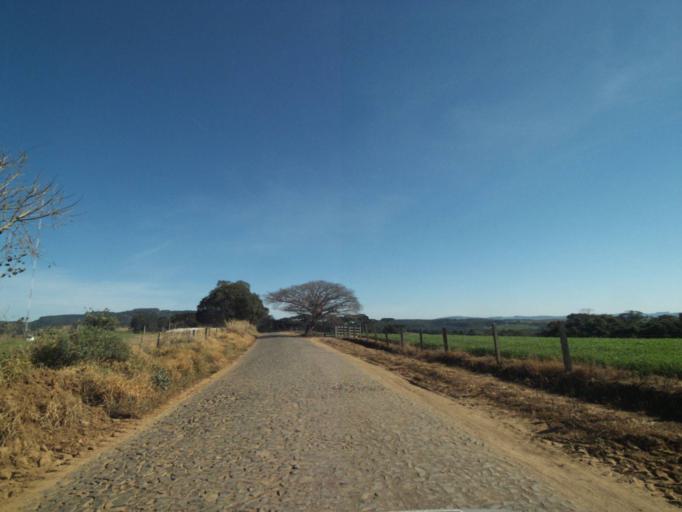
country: BR
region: Parana
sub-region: Tibagi
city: Tibagi
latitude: -24.5278
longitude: -50.4557
